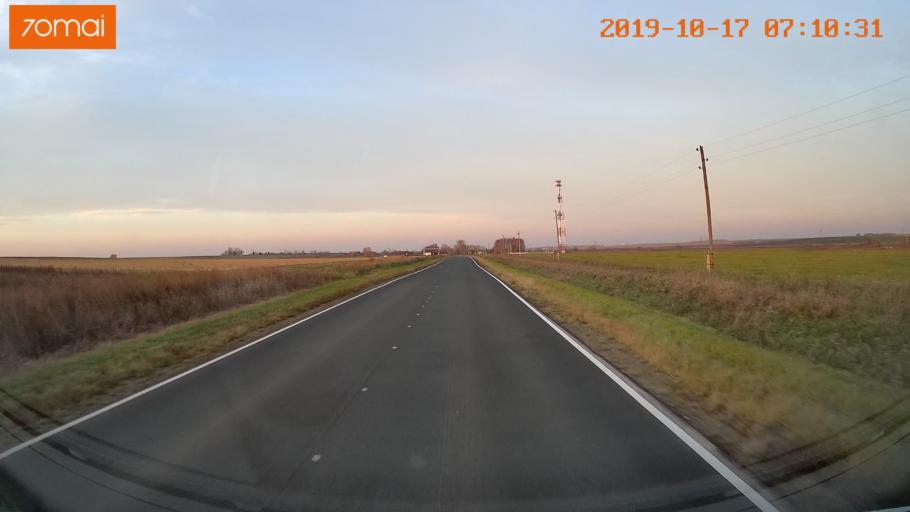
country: RU
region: Vladimir
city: Suzdal'
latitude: 56.4112
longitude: 40.3599
